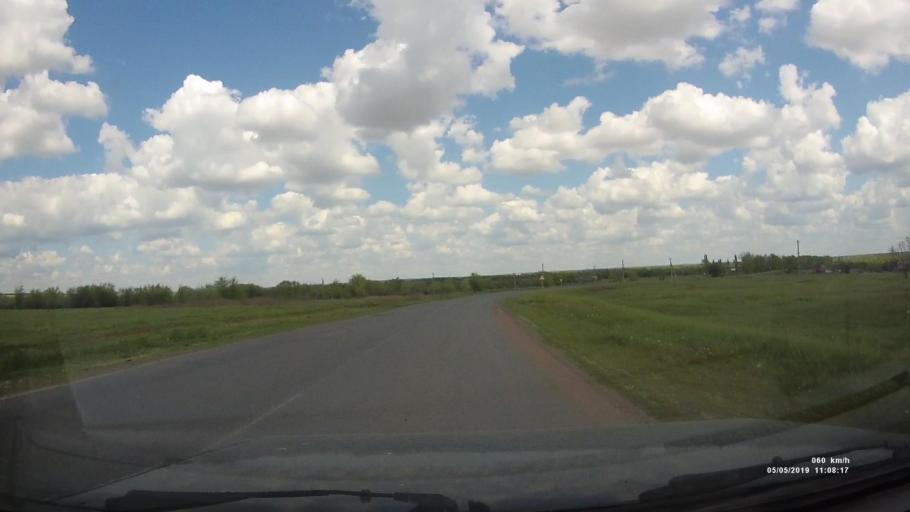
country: RU
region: Rostov
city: Ust'-Donetskiy
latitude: 47.7329
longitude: 40.9139
